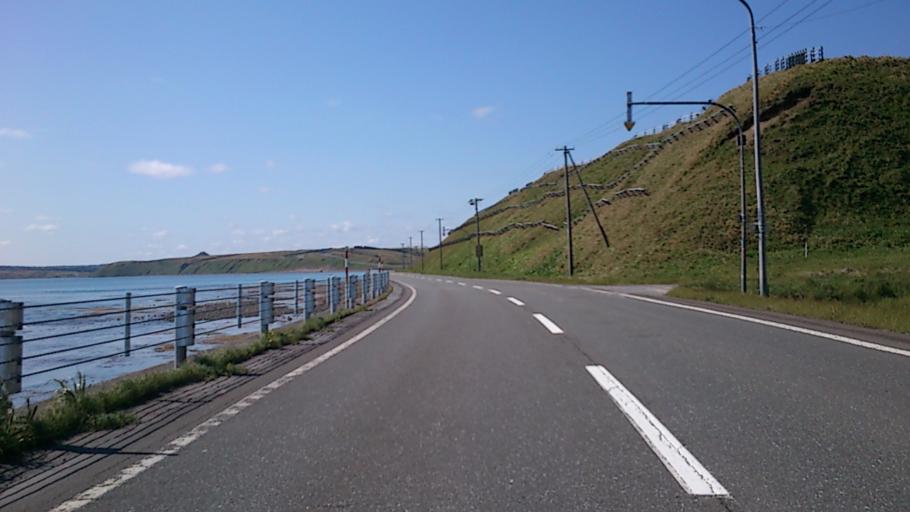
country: JP
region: Hokkaido
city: Makubetsu
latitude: 45.4957
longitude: 141.9670
